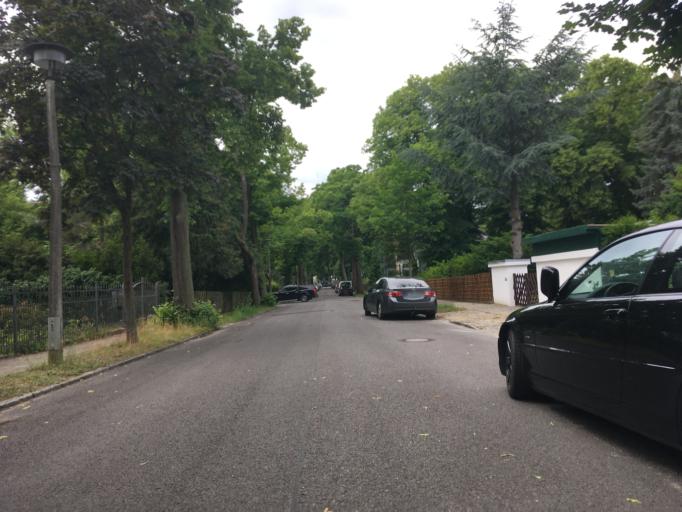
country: DE
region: Brandenburg
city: Erkner
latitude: 52.4267
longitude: 13.7317
